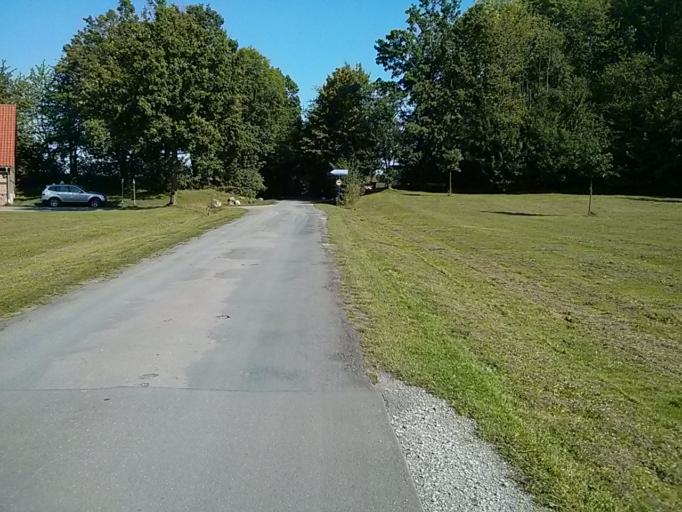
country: DE
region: North Rhine-Westphalia
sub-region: Regierungsbezirk Munster
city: Ennigerloh
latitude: 51.8693
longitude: 8.0877
